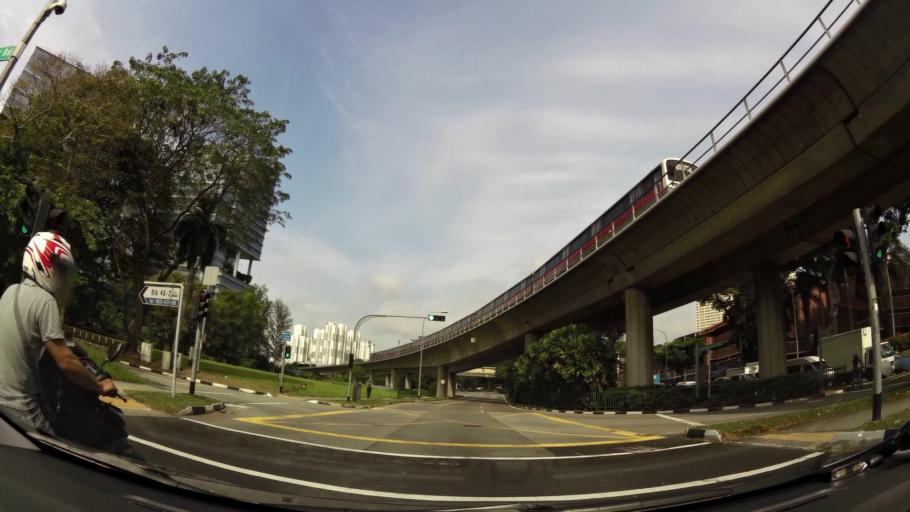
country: SG
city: Singapore
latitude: 1.3065
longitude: 103.7934
